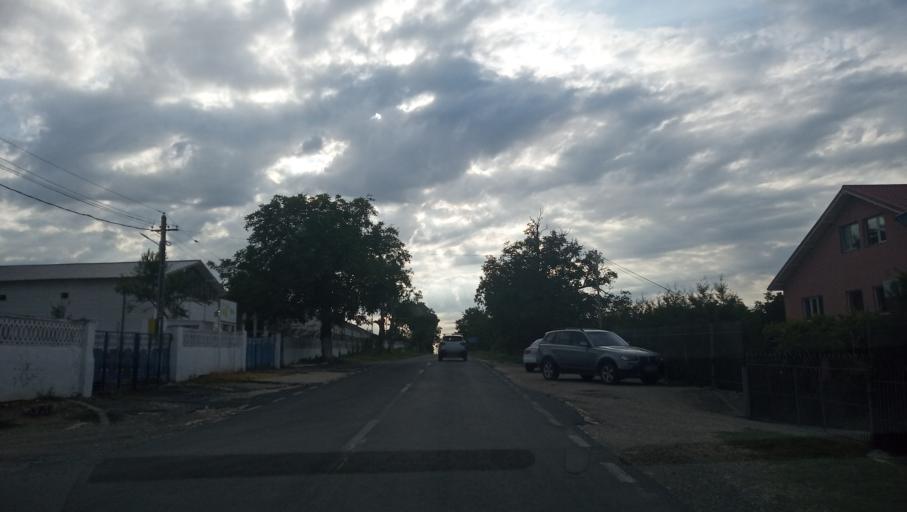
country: RO
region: Constanta
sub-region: Comuna Ostrov
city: Ostrov
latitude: 44.1024
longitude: 27.3773
